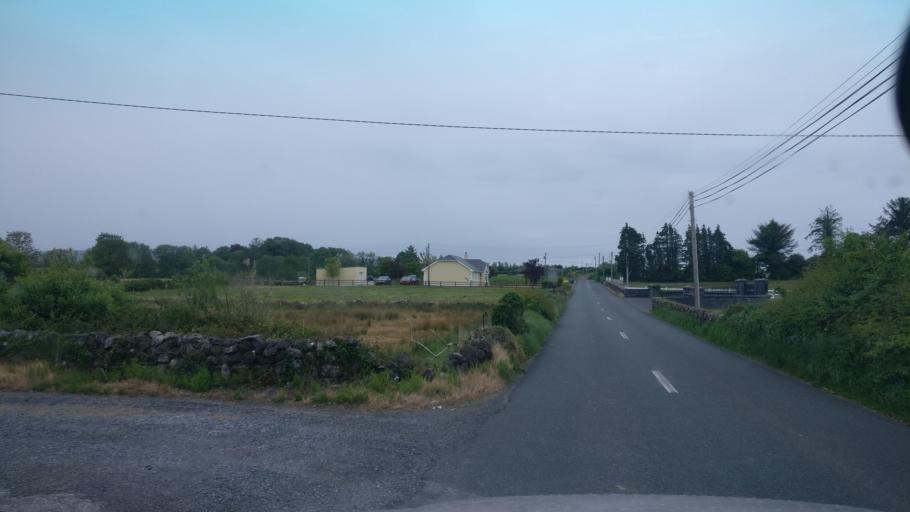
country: IE
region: Connaught
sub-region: County Galway
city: Gort
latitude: 53.0739
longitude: -8.7916
